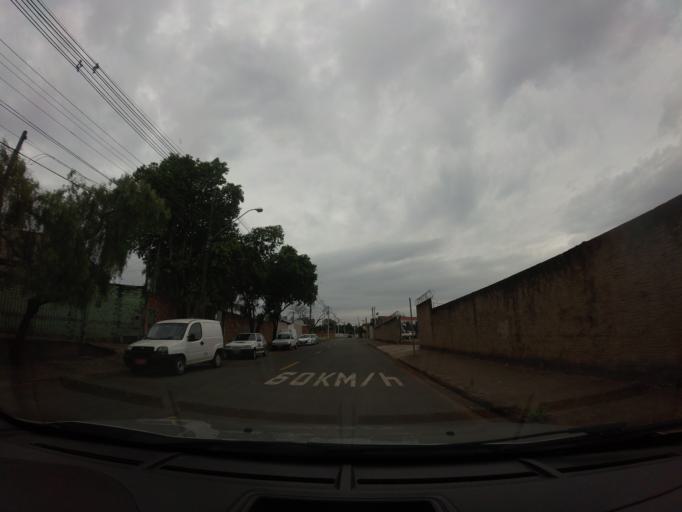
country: BR
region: Sao Paulo
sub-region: Piracicaba
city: Piracicaba
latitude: -22.7463
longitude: -47.5930
